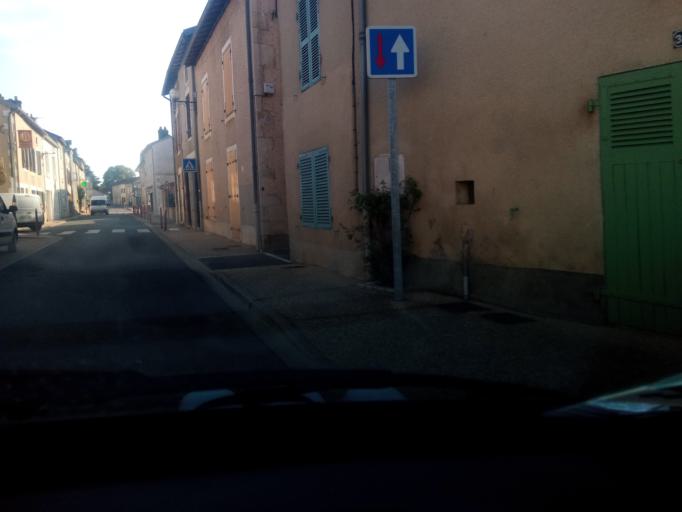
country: FR
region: Poitou-Charentes
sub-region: Departement de la Vienne
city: Lussac-les-Chateaux
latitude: 46.3453
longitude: 0.7057
